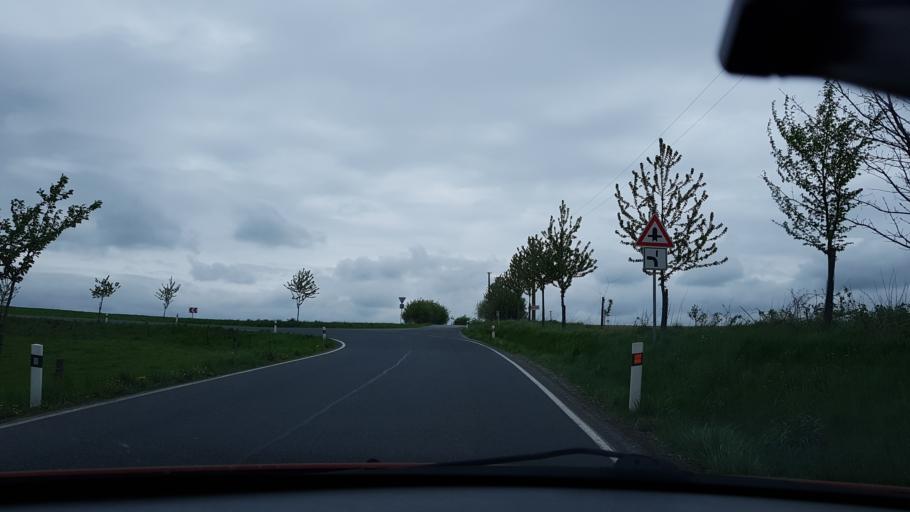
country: CZ
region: Olomoucky
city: Mikulovice
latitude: 50.3078
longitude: 17.3177
